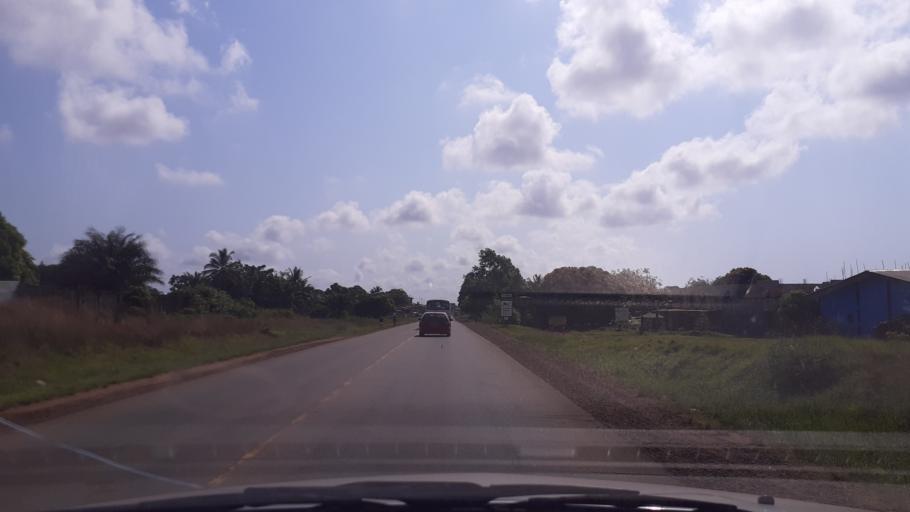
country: LR
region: Montserrado
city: Bensonville City
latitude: 6.2095
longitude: -10.5562
